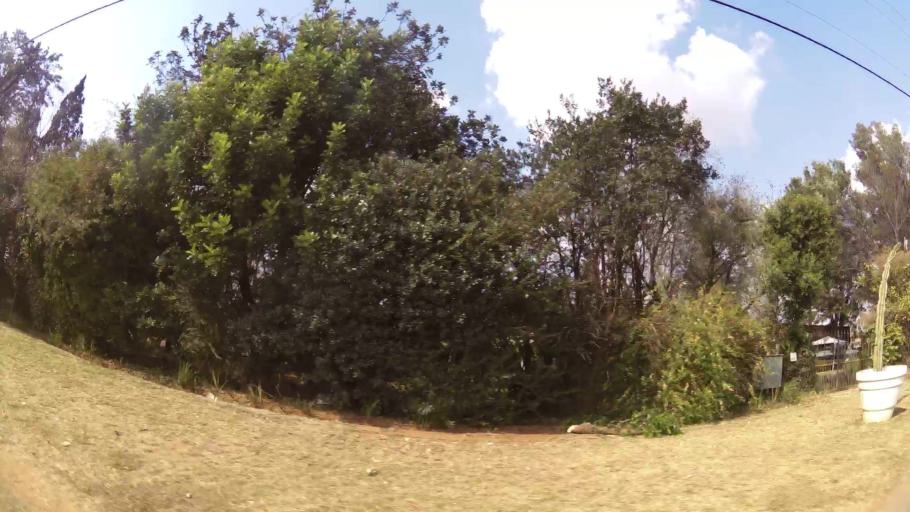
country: ZA
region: Mpumalanga
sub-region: Nkangala District Municipality
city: Delmas
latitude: -26.1493
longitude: 28.5490
